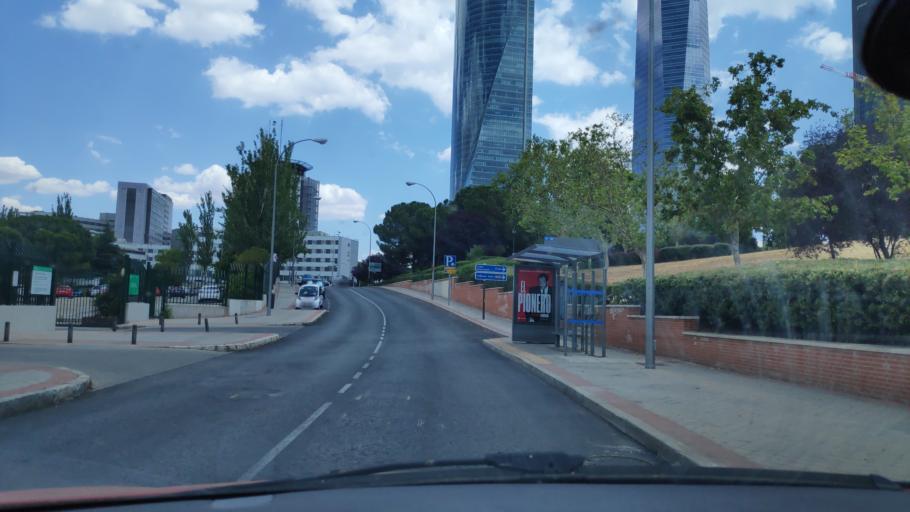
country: ES
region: Madrid
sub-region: Provincia de Madrid
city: Pinar de Chamartin
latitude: 40.4808
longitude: -3.6912
